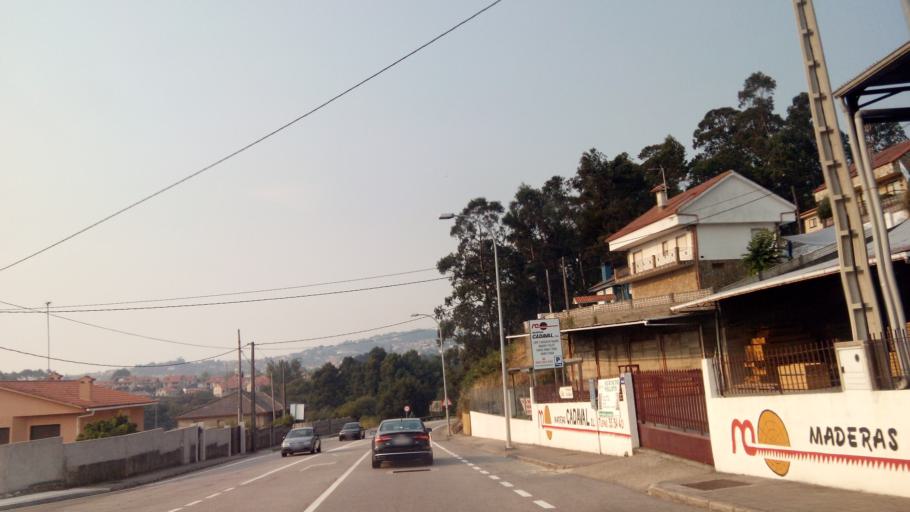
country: ES
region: Galicia
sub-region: Provincia de Pontevedra
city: Nigran
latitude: 42.1305
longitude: -8.8095
